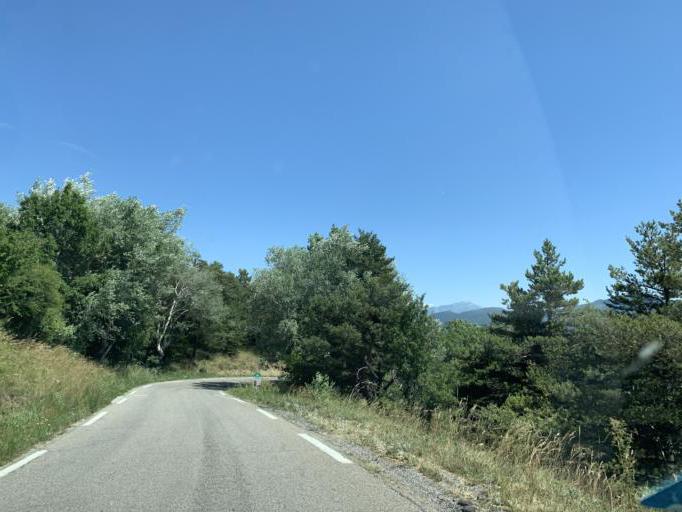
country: FR
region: Provence-Alpes-Cote d'Azur
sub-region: Departement des Hautes-Alpes
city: La Batie-Neuve
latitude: 44.5893
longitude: 6.1564
